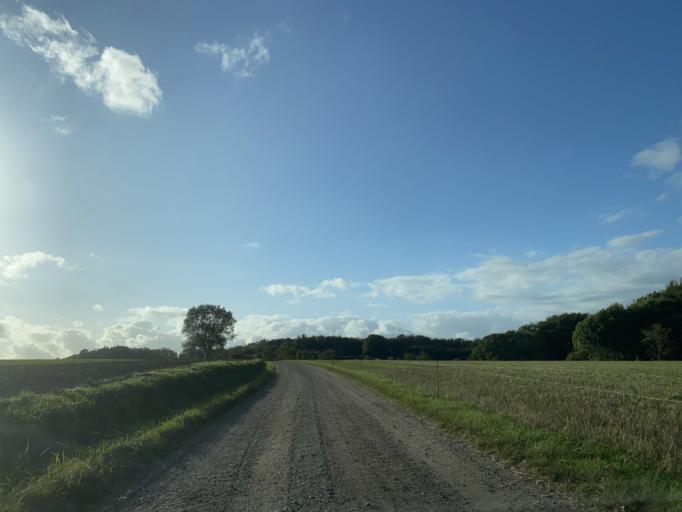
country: DK
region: Central Jutland
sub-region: Skanderborg Kommune
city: Ry
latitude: 56.1584
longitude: 9.7964
